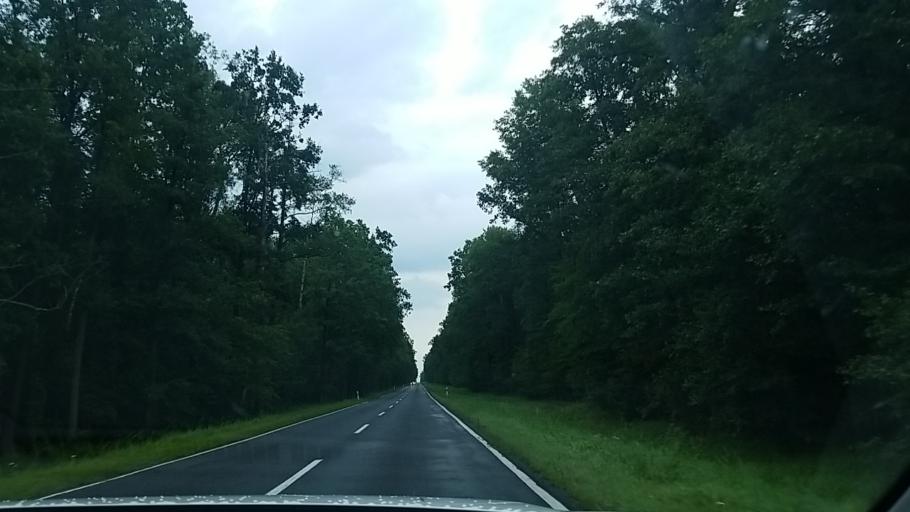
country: PL
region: Lublin Voivodeship
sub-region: Powiat wlodawski
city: Hansk
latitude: 51.4907
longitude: 23.3548
